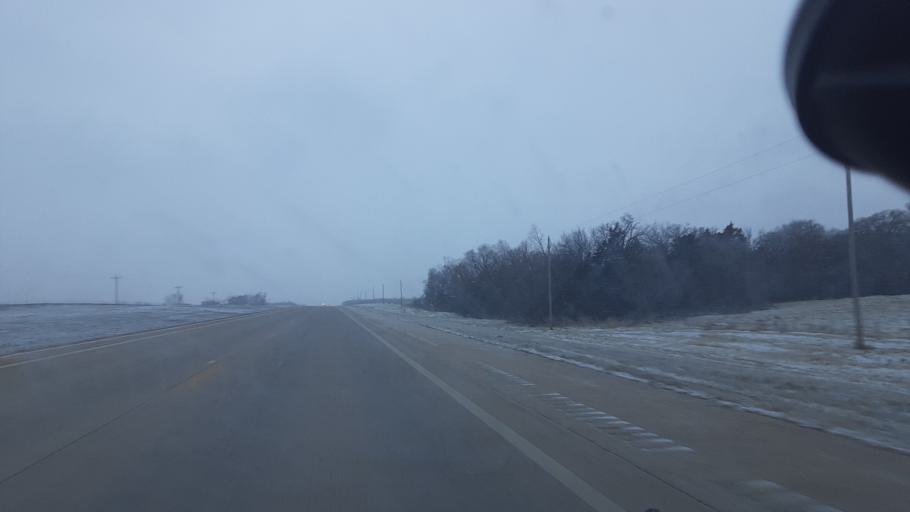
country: US
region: Oklahoma
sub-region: Payne County
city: Perkins
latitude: 35.9859
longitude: -97.1280
